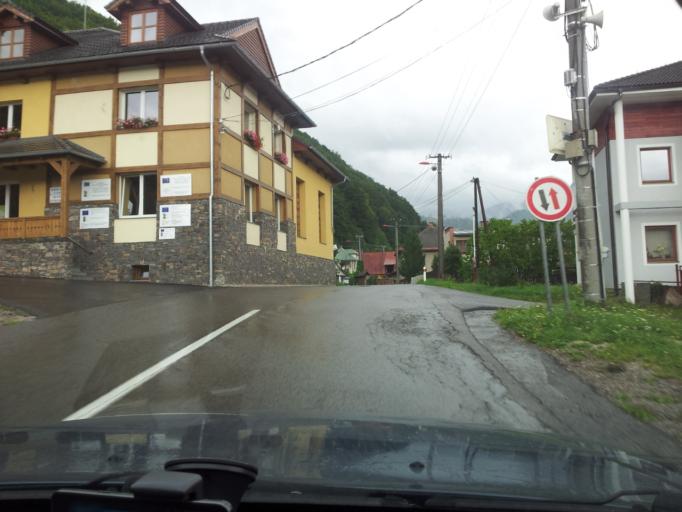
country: SK
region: Banskobystricky
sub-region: Okres Banska Bystrica
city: Brezno
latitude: 48.8538
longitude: 19.6329
